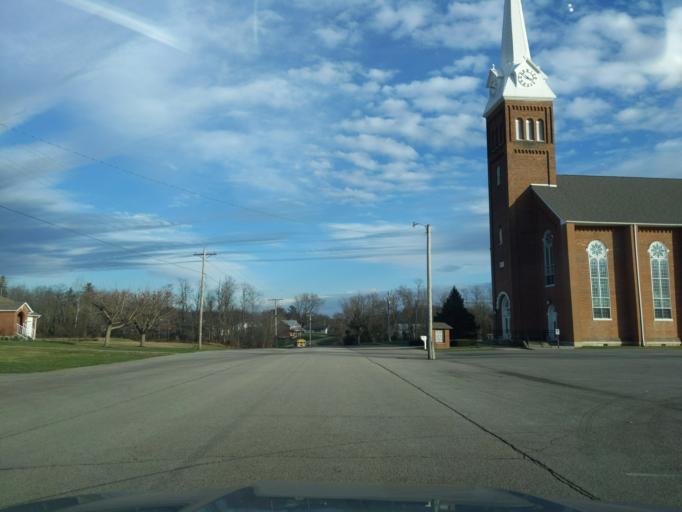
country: US
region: Indiana
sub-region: Decatur County
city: Greensburg
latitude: 39.2112
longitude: -85.4387
